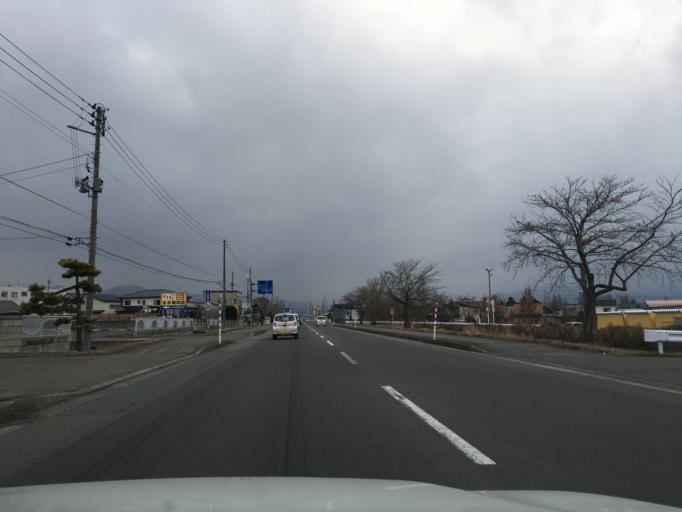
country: JP
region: Aomori
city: Kuroishi
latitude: 40.5898
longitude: 140.5690
